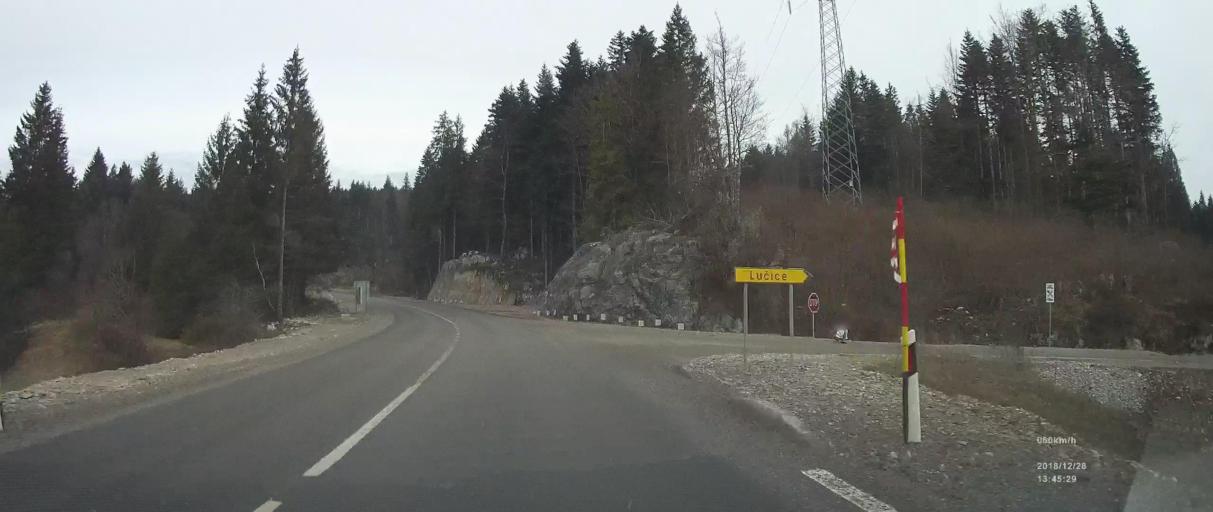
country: HR
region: Primorsko-Goranska
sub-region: Grad Delnice
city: Delnice
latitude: 45.3799
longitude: 14.7924
